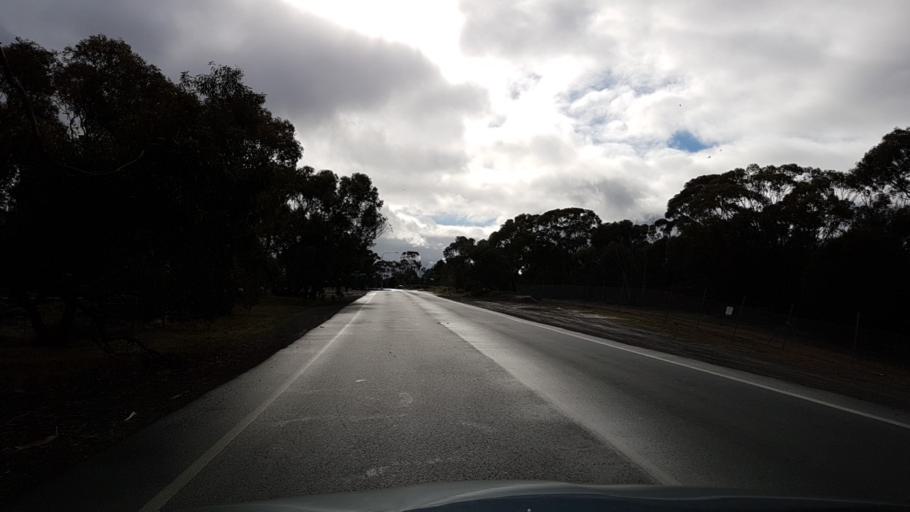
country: AU
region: South Australia
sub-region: Onkaparinga
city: Bedford Park
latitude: -35.0531
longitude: 138.5710
